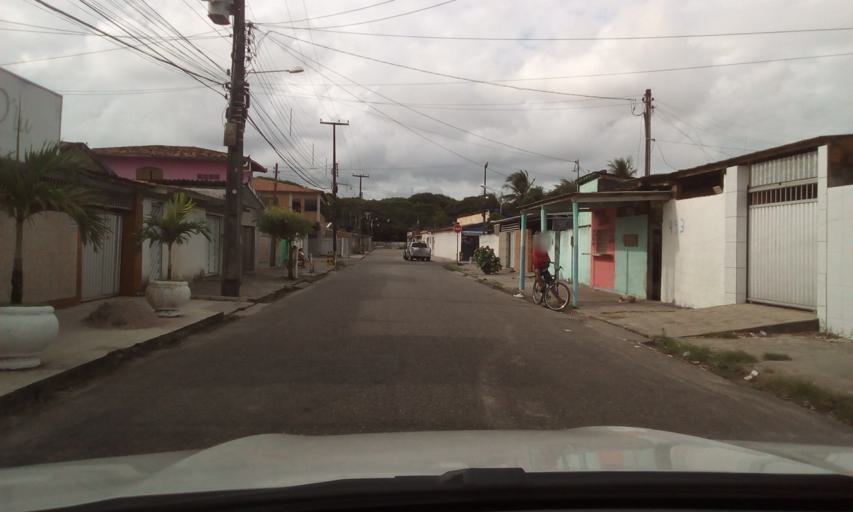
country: BR
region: Paraiba
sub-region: Joao Pessoa
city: Joao Pessoa
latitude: -7.1479
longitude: -34.8771
